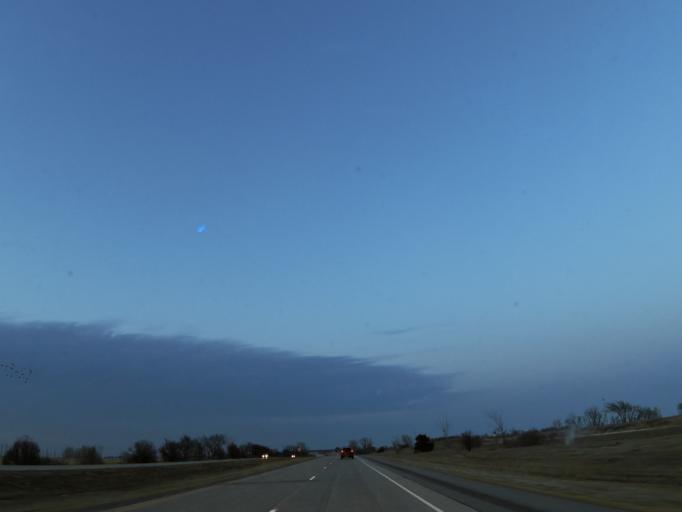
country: US
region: Minnesota
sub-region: Mower County
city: Grand Meadow
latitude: 43.8006
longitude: -92.5938
